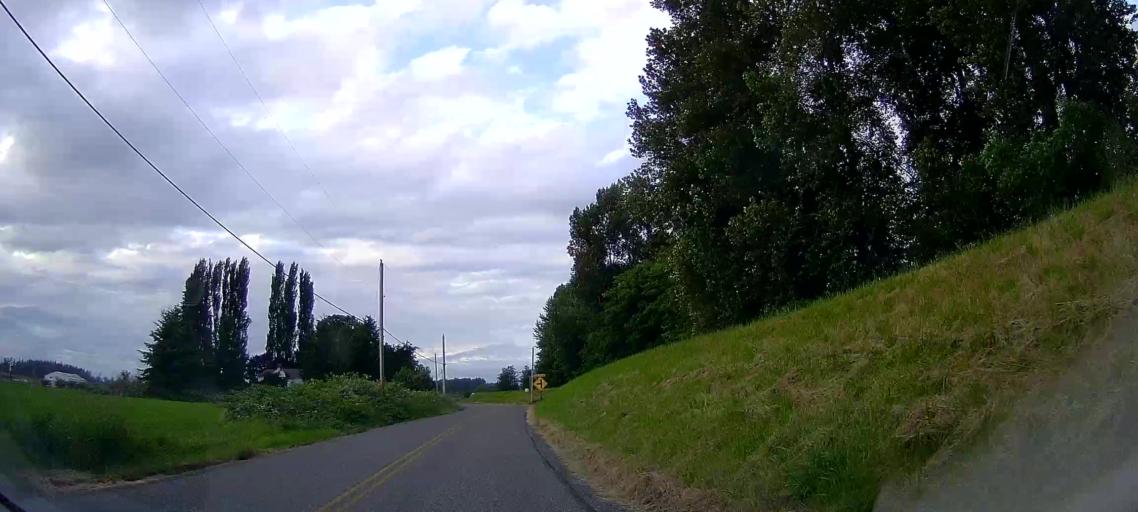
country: US
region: Washington
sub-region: Skagit County
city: Mount Vernon
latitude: 48.3539
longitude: -122.3628
